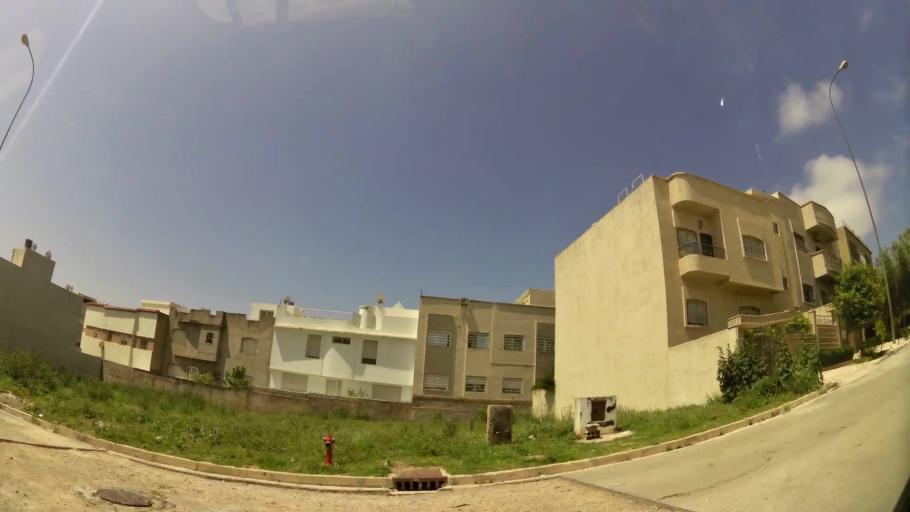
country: MA
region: Fes-Boulemane
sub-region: Fes
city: Fes
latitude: 34.0625
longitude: -5.0291
